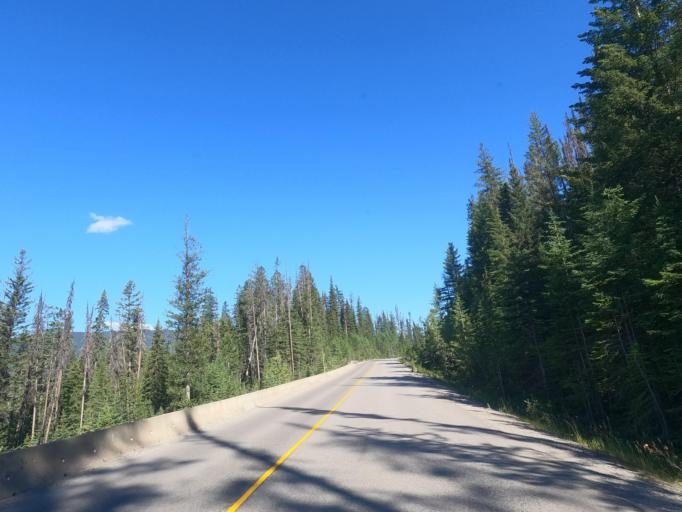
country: CA
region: Alberta
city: Lake Louise
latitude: 51.3849
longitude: -116.5353
